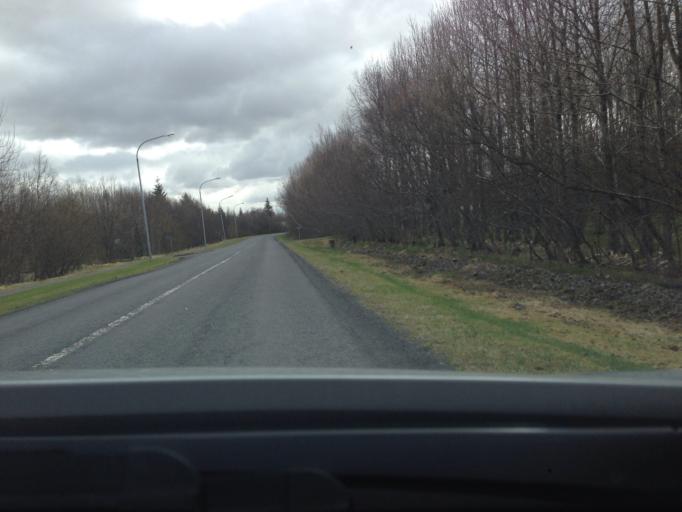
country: IS
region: South
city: Selfoss
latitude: 64.1183
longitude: -20.5015
